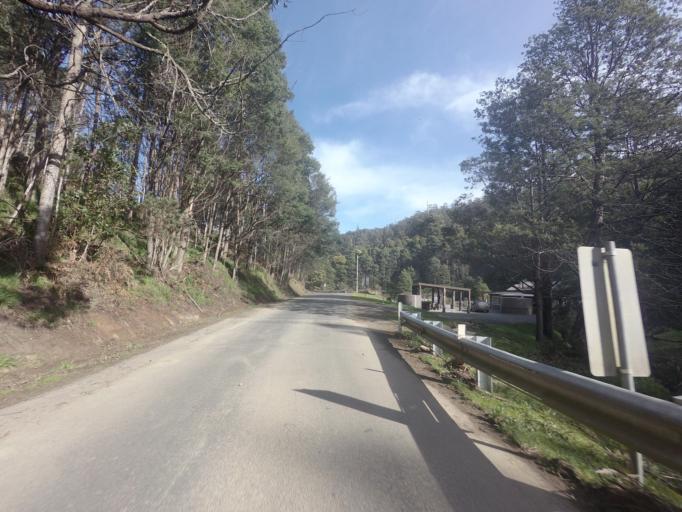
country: AU
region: Tasmania
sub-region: Huon Valley
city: Huonville
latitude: -43.0354
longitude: 147.1434
